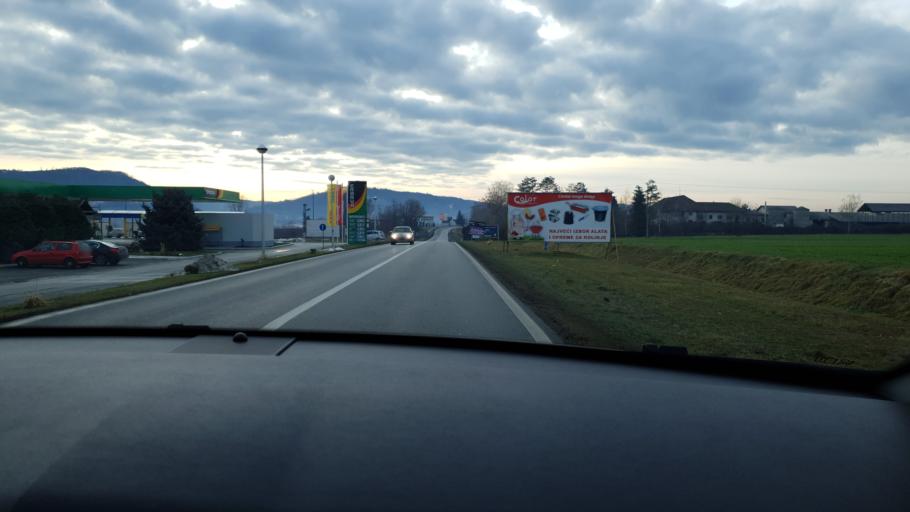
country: HR
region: Pozesko-Slavonska
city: Vidovci
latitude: 45.3443
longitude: 17.7150
